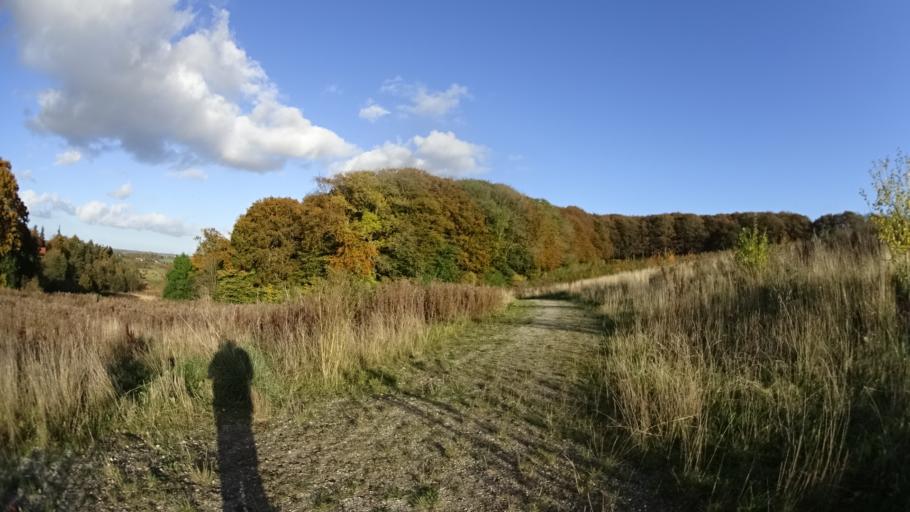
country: DK
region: Central Jutland
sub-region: Arhus Kommune
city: Kolt
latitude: 56.1231
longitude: 10.0457
